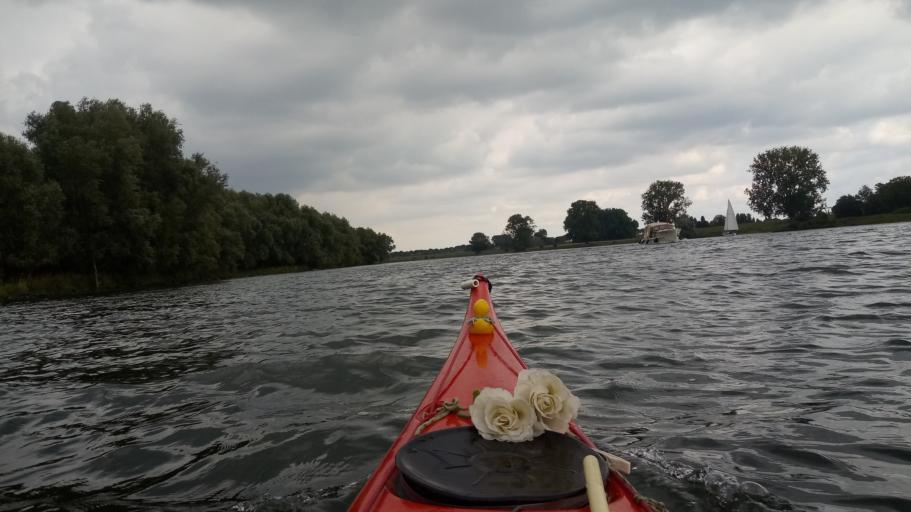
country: NL
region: North Brabant
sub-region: Gemeente 's-Hertogenbosch
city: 's-Hertogenbosch
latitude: 51.7547
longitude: 5.3481
